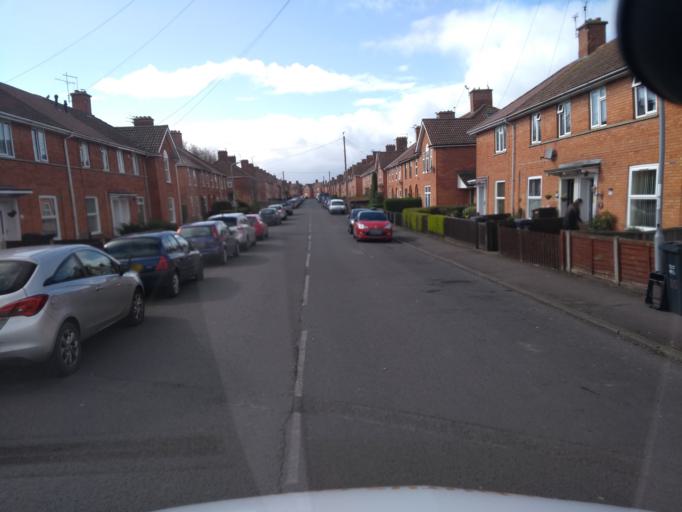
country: GB
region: England
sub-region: Somerset
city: Bridgwater
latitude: 51.1339
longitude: -3.0108
